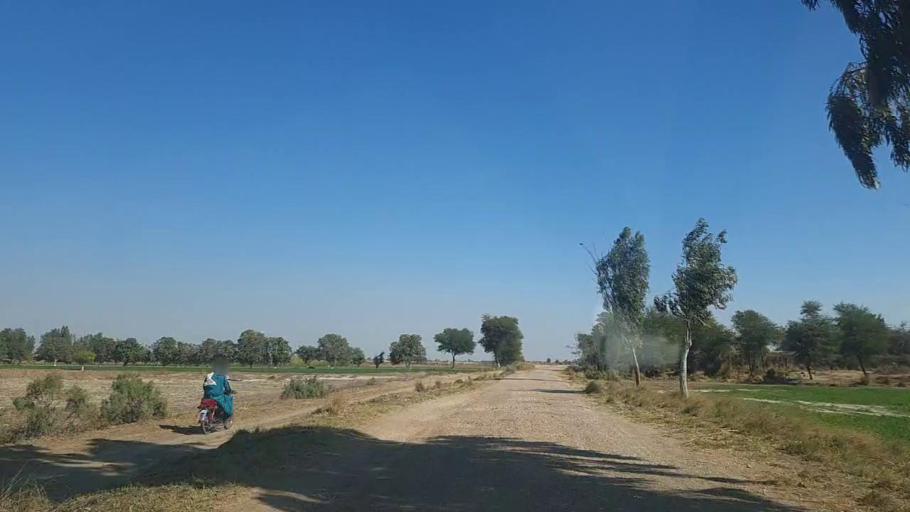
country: PK
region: Sindh
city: Sanghar
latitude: 26.2093
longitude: 68.8833
